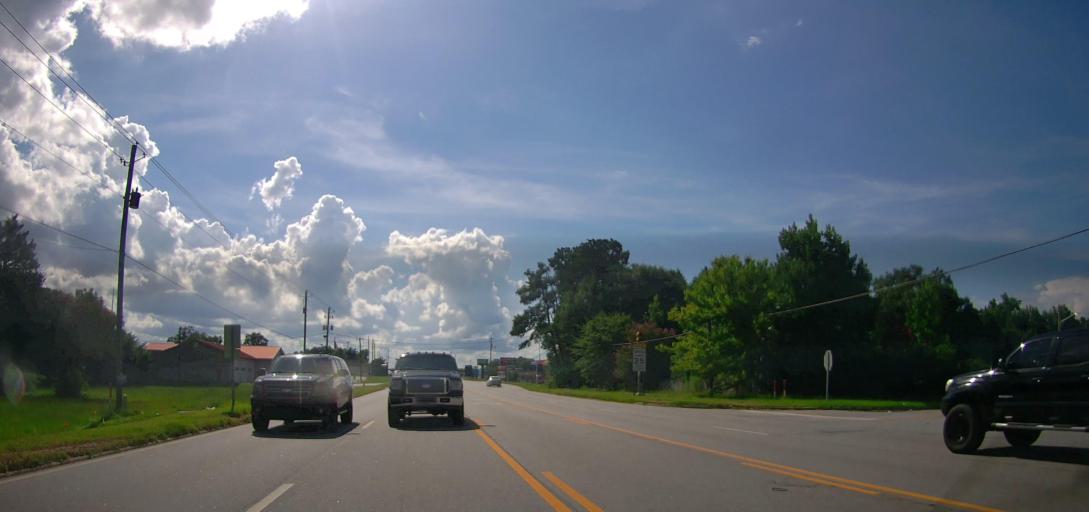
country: US
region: Alabama
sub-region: Russell County
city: Ladonia
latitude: 32.4689
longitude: -85.0816
